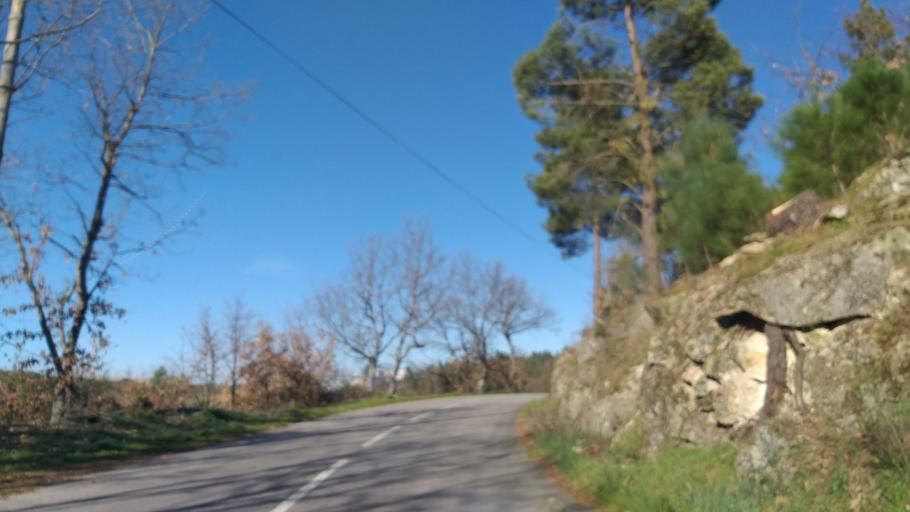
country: PT
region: Guarda
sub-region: Celorico da Beira
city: Celorico da Beira
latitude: 40.5977
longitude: -7.3627
